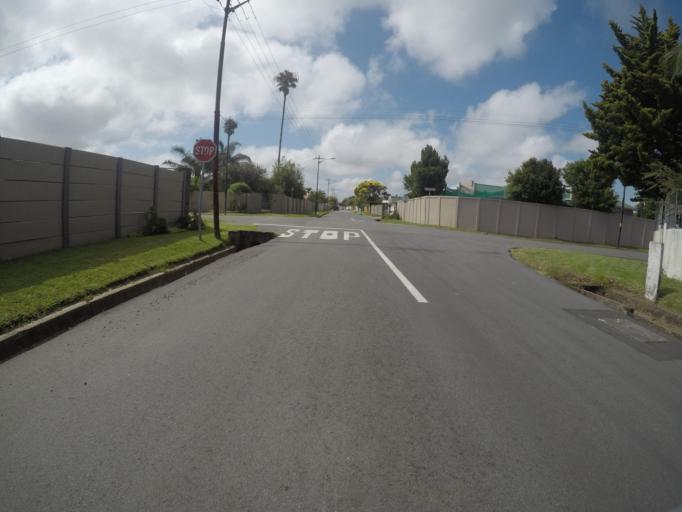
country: ZA
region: Eastern Cape
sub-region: Buffalo City Metropolitan Municipality
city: East London
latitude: -32.9817
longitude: 27.9080
